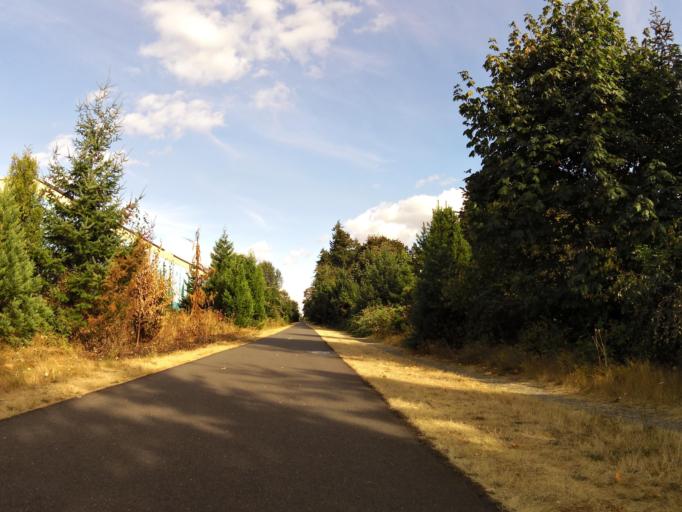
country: US
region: Washington
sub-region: Thurston County
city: Lacey
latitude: 47.0397
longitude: -122.8446
